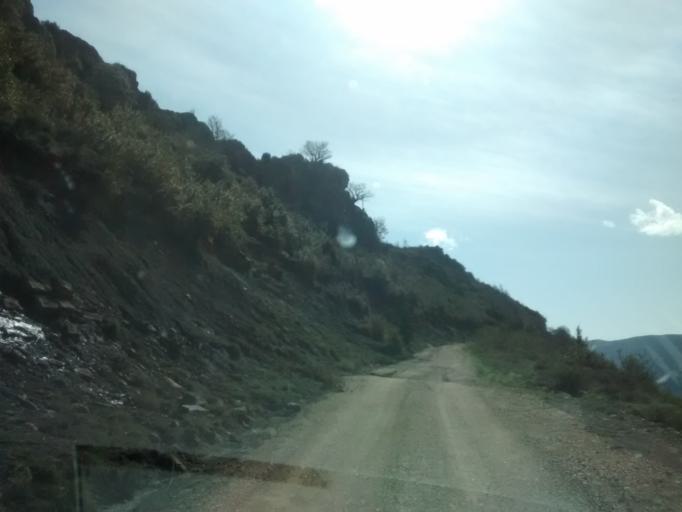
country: ES
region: Aragon
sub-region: Provincia de Huesca
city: Arguis
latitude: 42.3280
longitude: -0.3999
